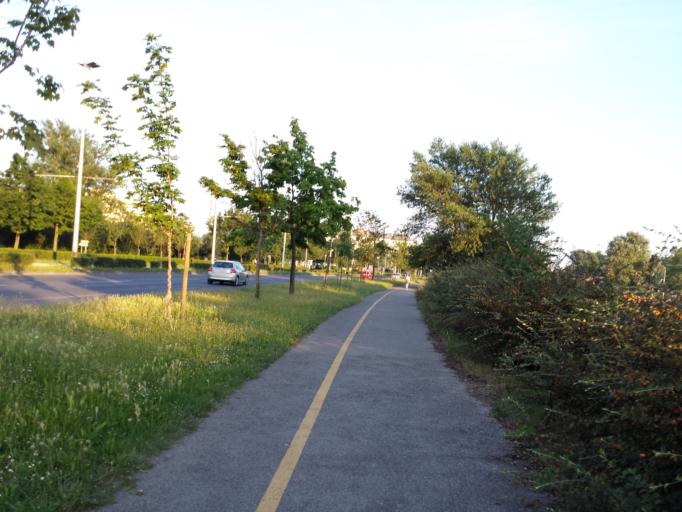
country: HR
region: Grad Zagreb
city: Novi Zagreb
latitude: 45.7907
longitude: 16.0031
